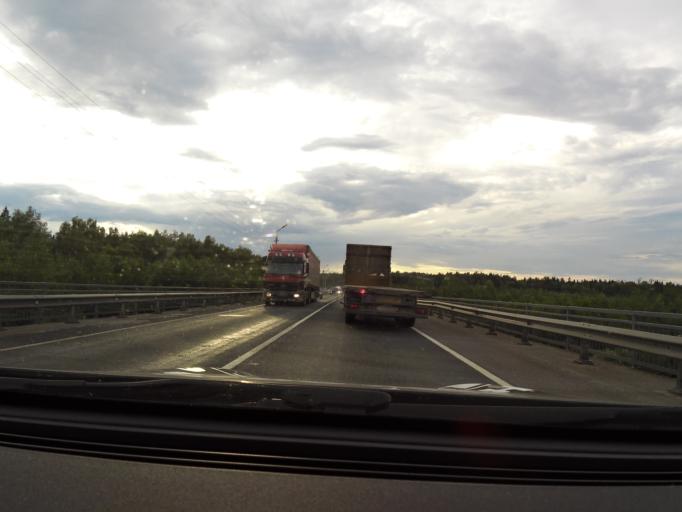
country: RU
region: Vladimir
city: Raduzhnyy
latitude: 56.0631
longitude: 40.3692
